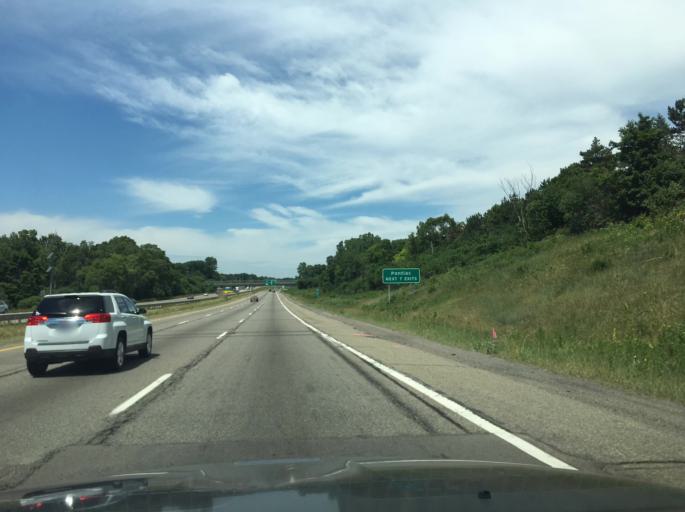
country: US
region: Michigan
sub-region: Oakland County
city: Bloomfield Hills
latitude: 42.6092
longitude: -83.2176
